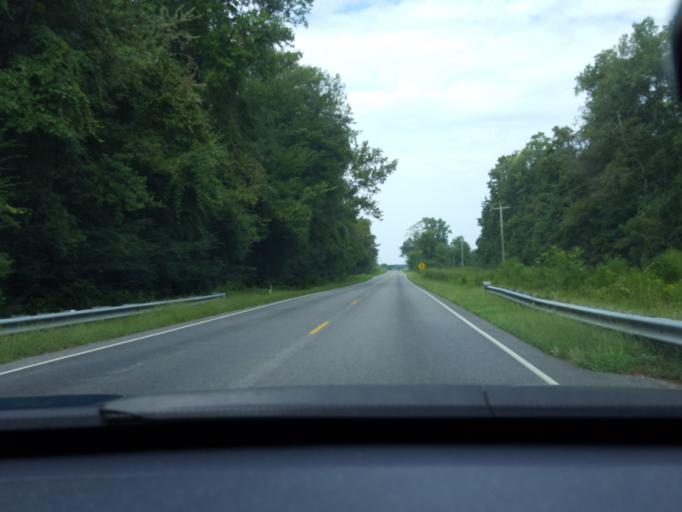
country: US
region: North Carolina
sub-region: Chowan County
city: Edenton
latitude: 36.1039
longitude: -76.6336
